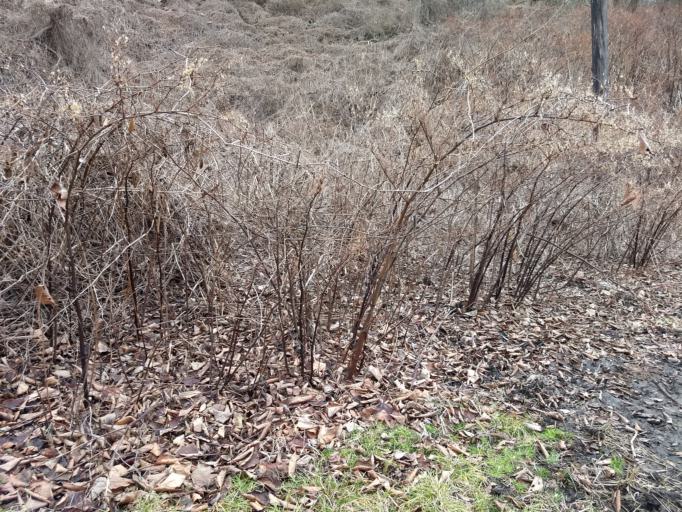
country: US
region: Pennsylvania
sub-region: Allegheny County
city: Bloomfield
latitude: 40.4217
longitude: -79.9487
